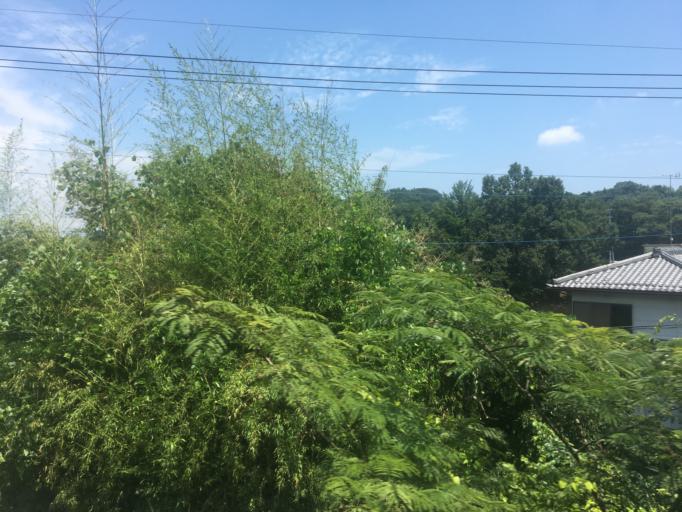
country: JP
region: Saitama
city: Yorii
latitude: 36.0980
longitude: 139.1939
